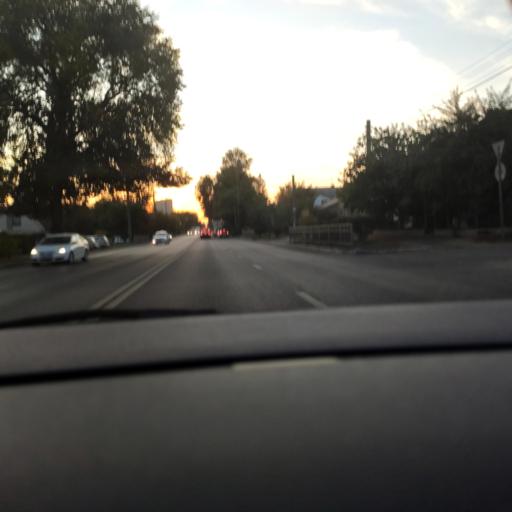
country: RU
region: Voronezj
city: Voronezh
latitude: 51.6942
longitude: 39.1601
